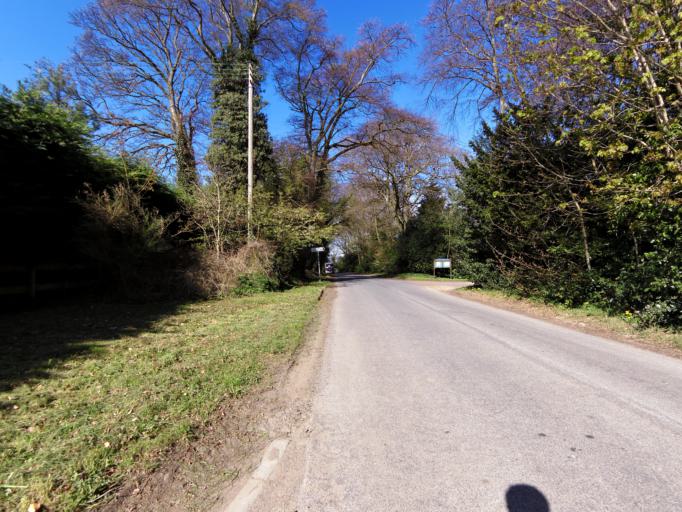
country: GB
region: Scotland
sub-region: Dundee City
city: Dundee
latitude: 56.4084
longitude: -3.0246
